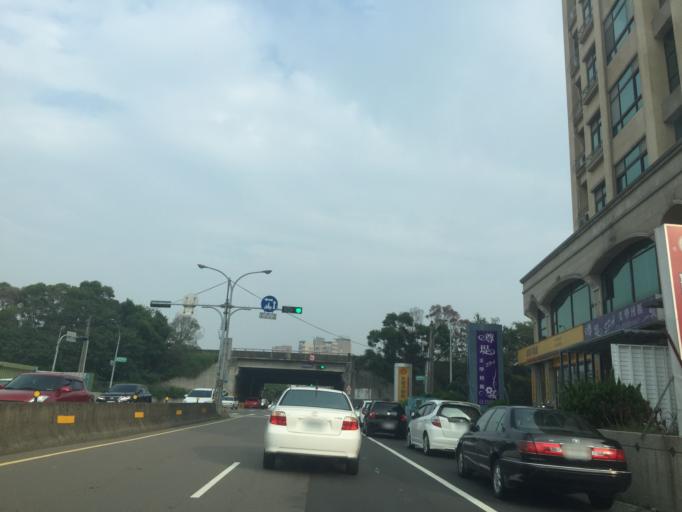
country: TW
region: Taiwan
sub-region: Hsinchu
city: Zhubei
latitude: 24.8210
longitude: 121.0142
